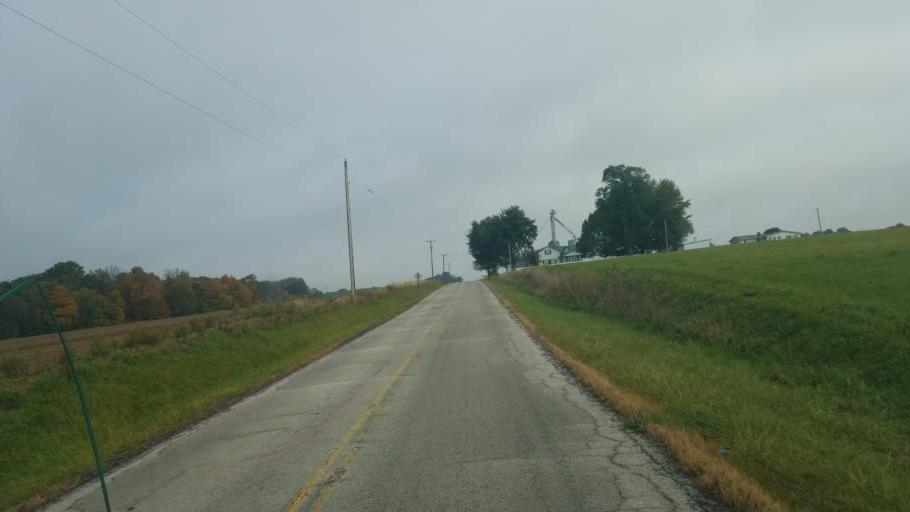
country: US
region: Ohio
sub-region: Richland County
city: Ontario
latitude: 40.7191
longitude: -82.6358
